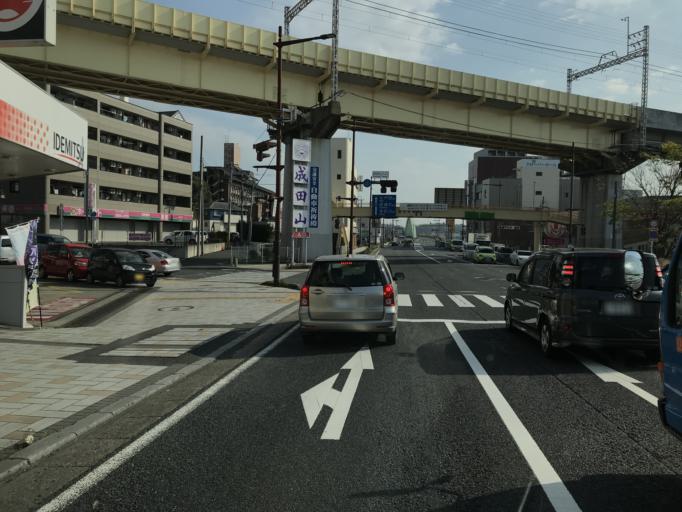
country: JP
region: Chiba
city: Narita
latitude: 35.7786
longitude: 140.3218
